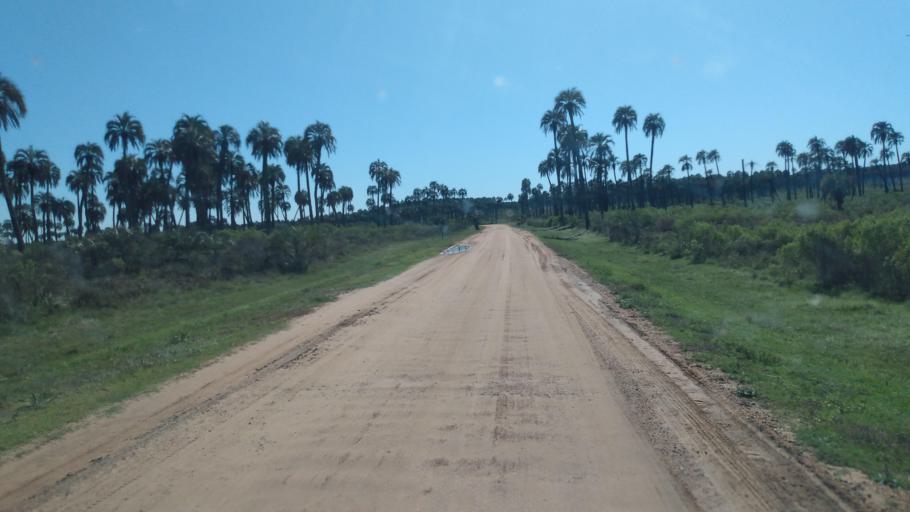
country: AR
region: Entre Rios
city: Ubajay
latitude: -31.8541
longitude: -58.3184
